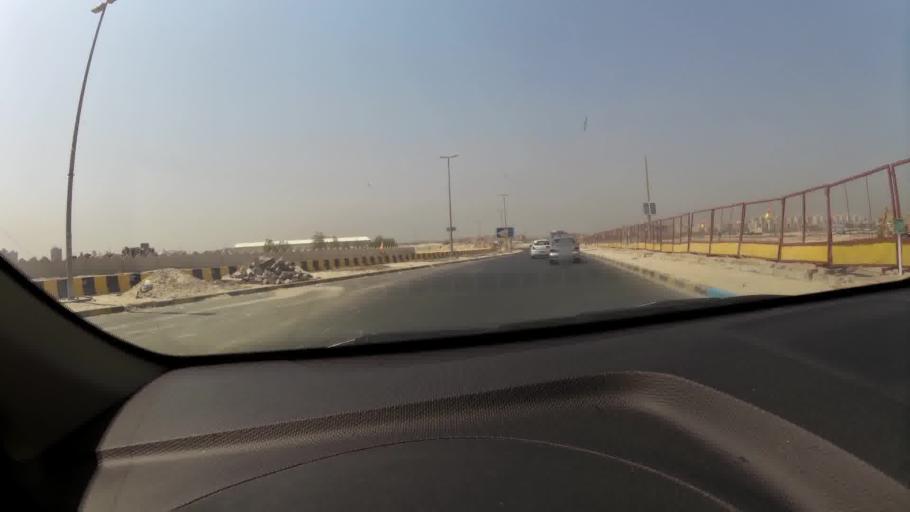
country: KW
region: Al Farwaniyah
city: Al Farwaniyah
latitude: 29.2574
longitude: 47.9535
